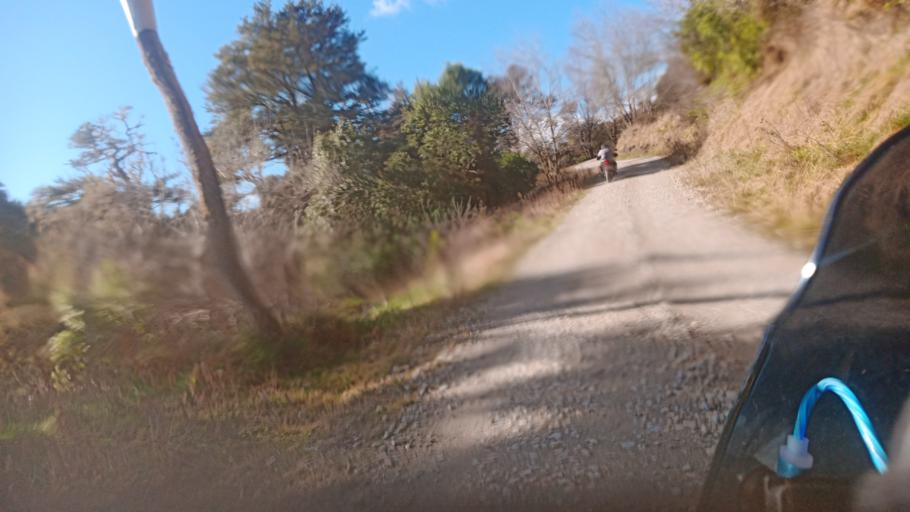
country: NZ
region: Hawke's Bay
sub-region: Wairoa District
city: Wairoa
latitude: -38.6634
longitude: 177.5119
